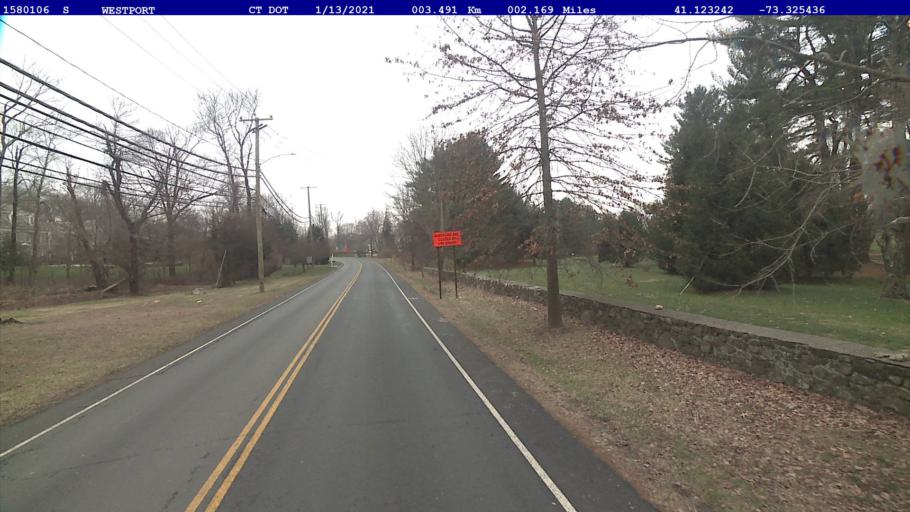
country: US
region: Connecticut
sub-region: Fairfield County
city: Westport
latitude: 41.1232
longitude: -73.3254
